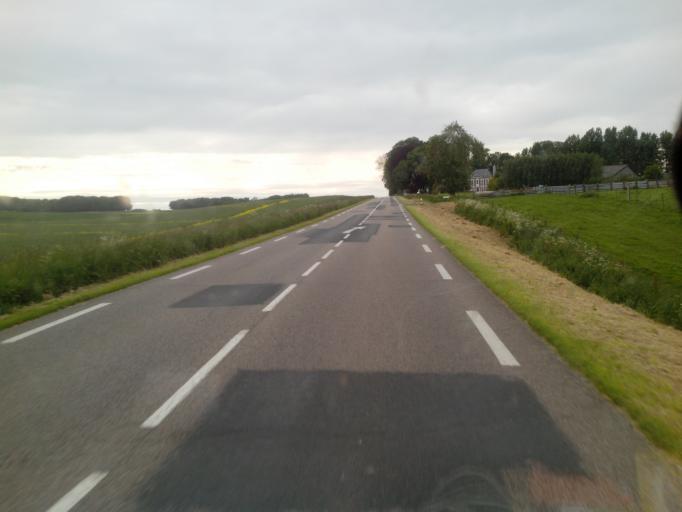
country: FR
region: Haute-Normandie
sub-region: Departement de la Seine-Maritime
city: Fauville-en-Caux
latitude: 49.6826
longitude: 0.5558
